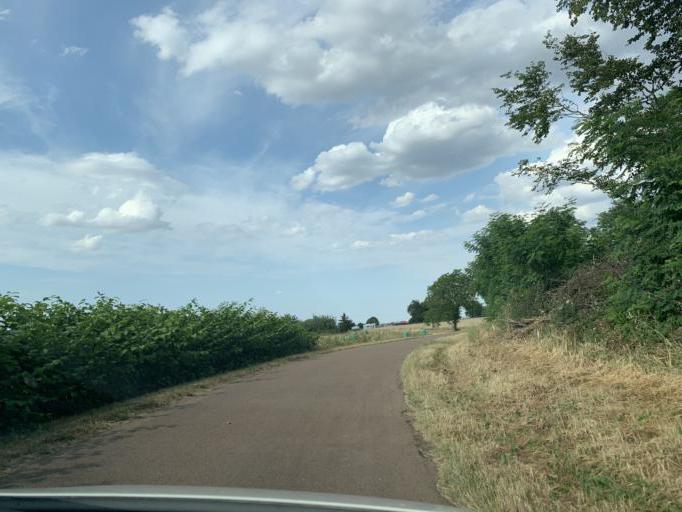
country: FR
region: Bourgogne
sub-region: Departement de l'Yonne
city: Fontenailles
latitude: 47.5143
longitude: 3.4261
